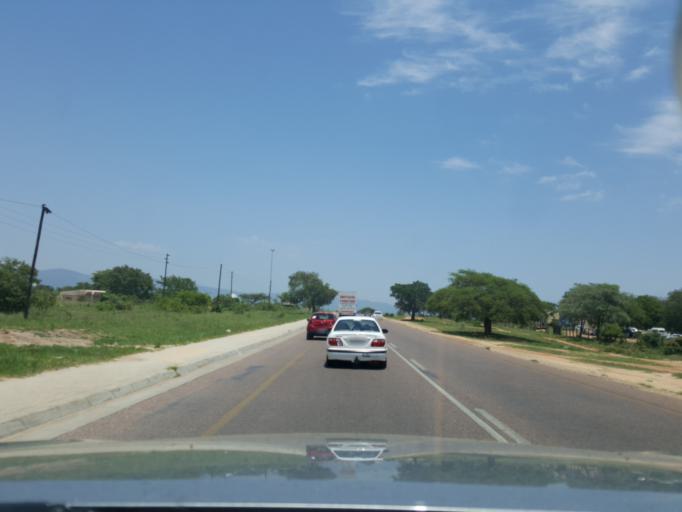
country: ZA
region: Limpopo
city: Thulamahashi
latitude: -24.7838
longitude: 31.0699
